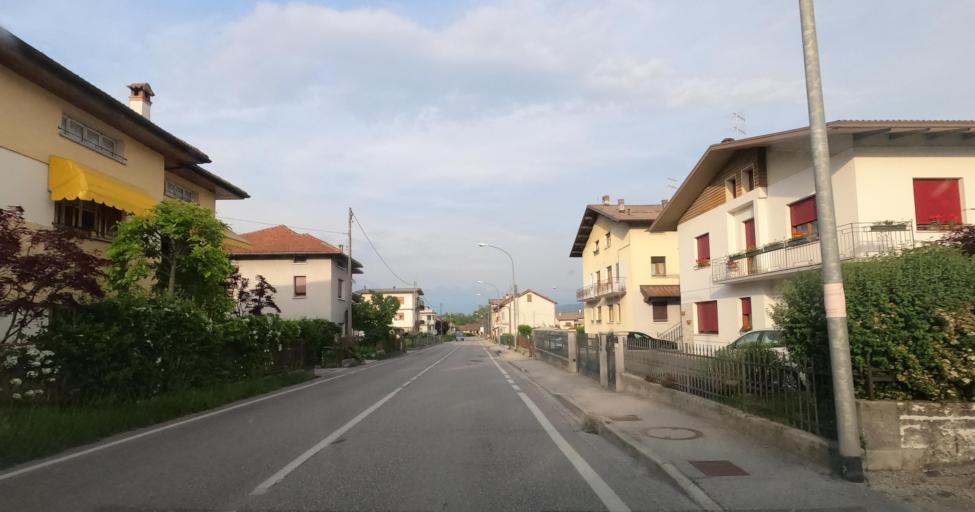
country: IT
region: Veneto
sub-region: Provincia di Belluno
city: Belluno
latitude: 46.1412
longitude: 12.1875
